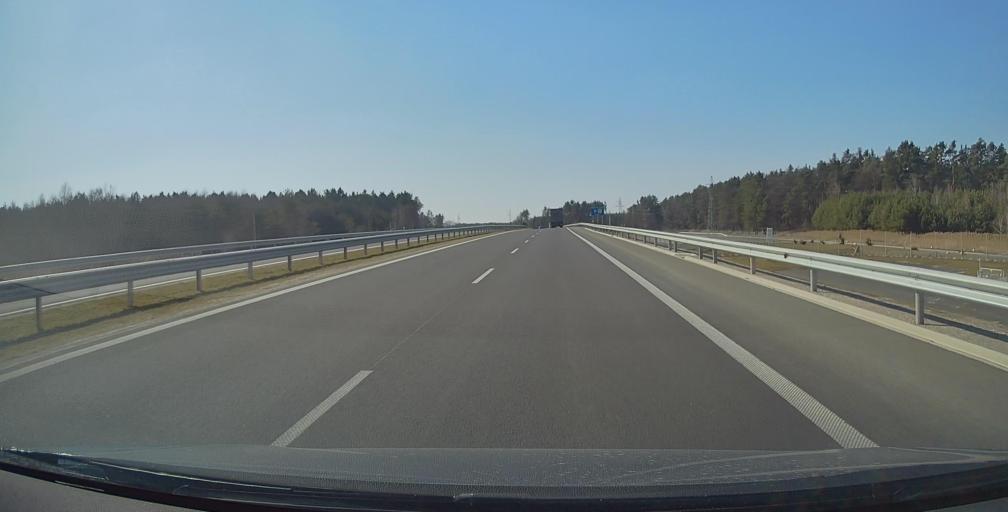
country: PL
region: Subcarpathian Voivodeship
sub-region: Powiat nizanski
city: Konczyce
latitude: 50.4322
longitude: 22.1347
